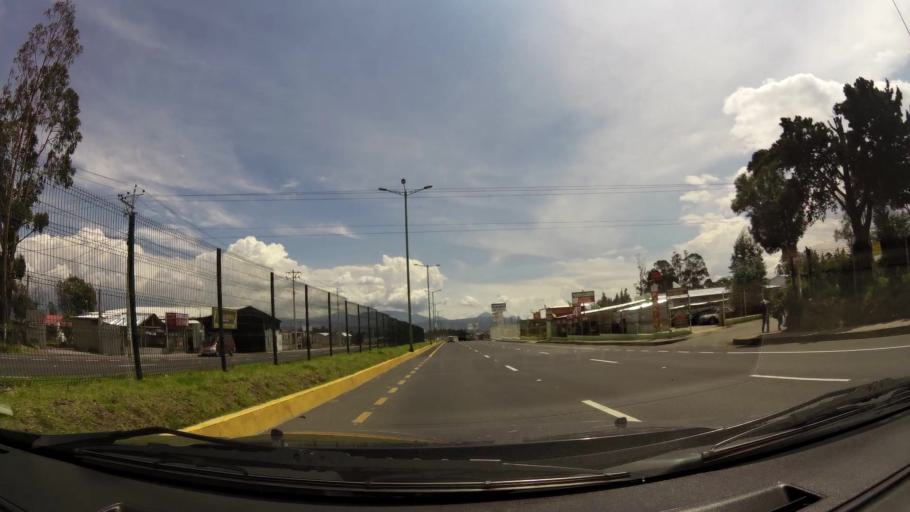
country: EC
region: Pichincha
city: Sangolqui
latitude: -0.2016
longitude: -78.3355
